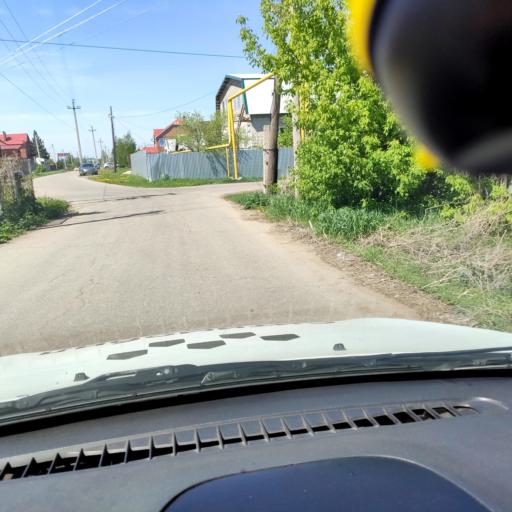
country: RU
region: Samara
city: Tol'yatti
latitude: 53.5724
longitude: 49.3242
